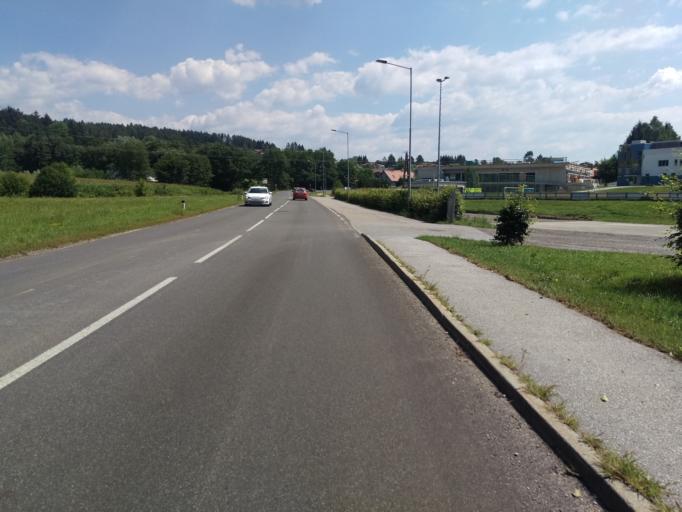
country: AT
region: Styria
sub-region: Politischer Bezirk Graz-Umgebung
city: Sankt Radegund bei Graz
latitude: 47.1417
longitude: 15.4954
